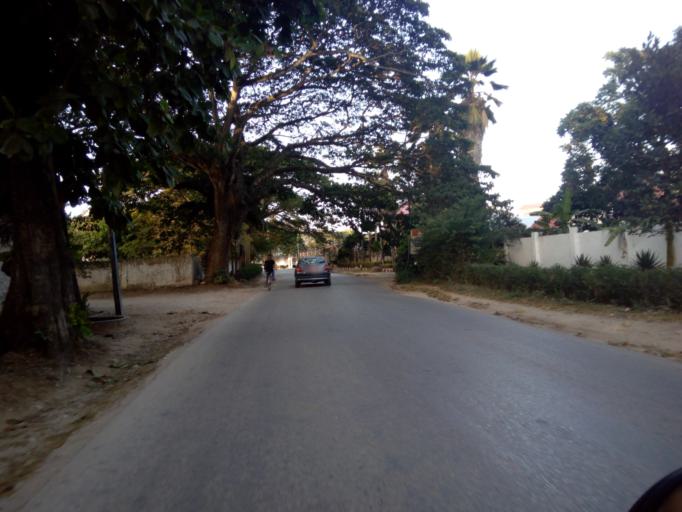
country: TZ
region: Zanzibar Urban/West
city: Zanzibar
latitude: -6.2025
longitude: 39.2104
